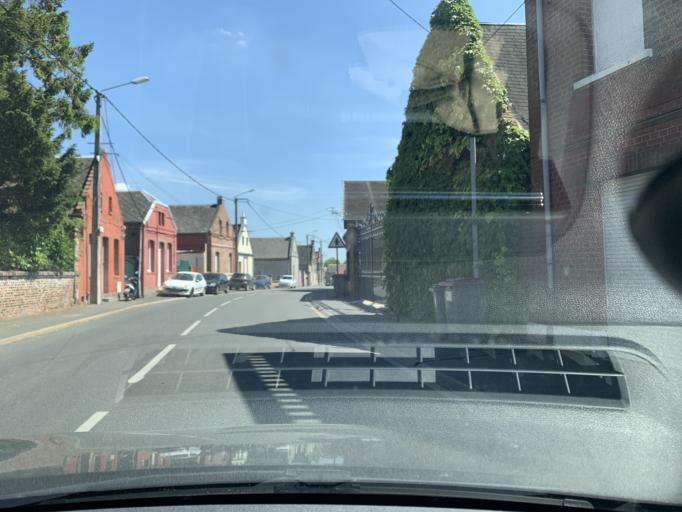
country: FR
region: Nord-Pas-de-Calais
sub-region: Departement du Nord
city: Fontaine-au-Pire
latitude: 50.1333
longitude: 3.3767
